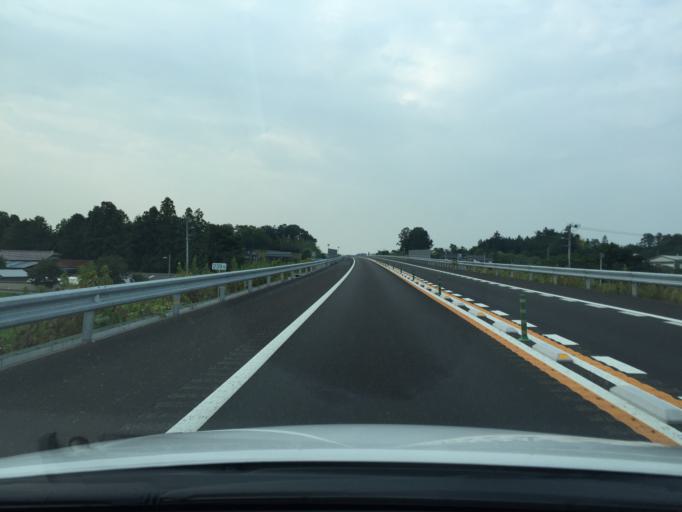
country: JP
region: Fukushima
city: Namie
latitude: 37.5614
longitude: 140.9454
